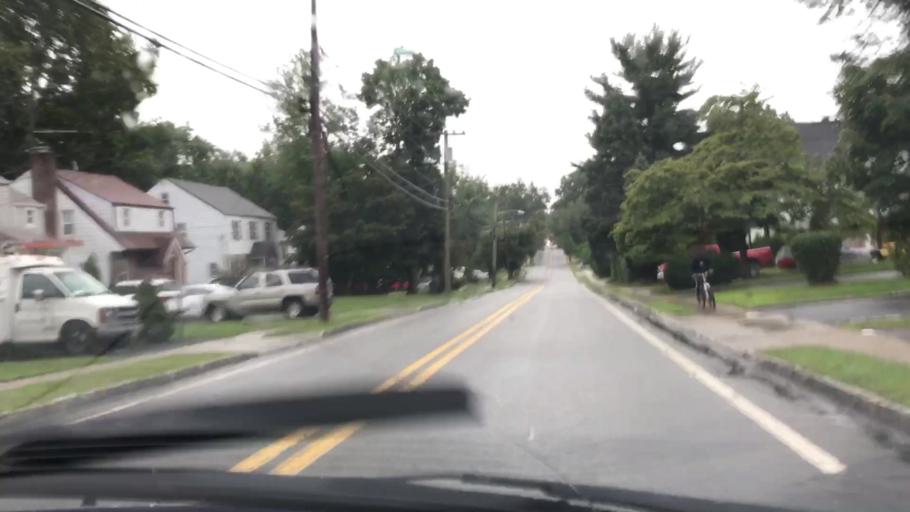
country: US
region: New Jersey
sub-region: Bergen County
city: Englewood
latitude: 40.9029
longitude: -73.9843
